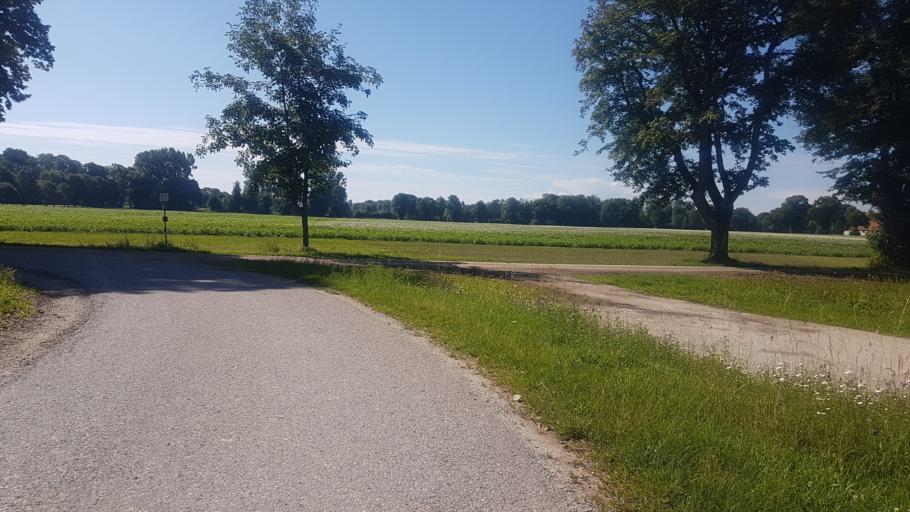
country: DE
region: Bavaria
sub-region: Upper Bavaria
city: Bergheim
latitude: 48.7363
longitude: 11.2631
